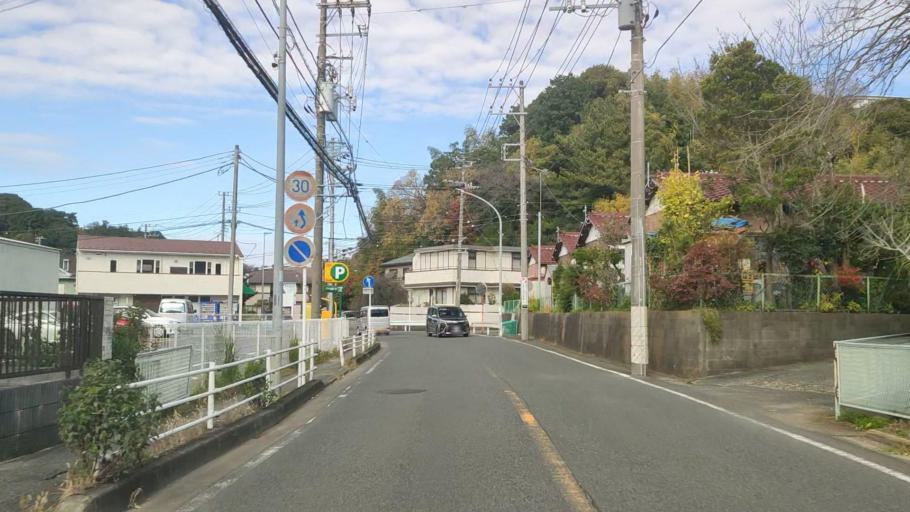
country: JP
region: Kanagawa
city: Yokohama
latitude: 35.4337
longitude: 139.5482
